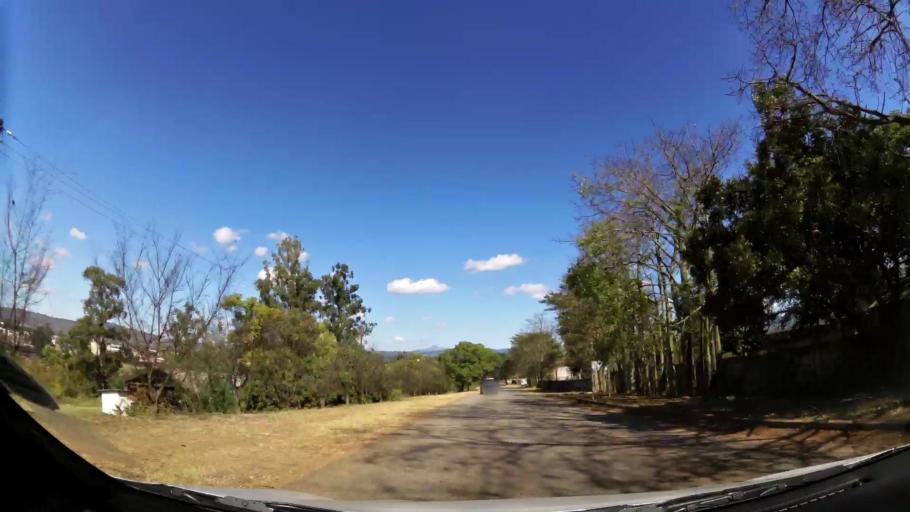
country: ZA
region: Limpopo
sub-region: Mopani District Municipality
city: Tzaneen
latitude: -23.8210
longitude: 30.1691
